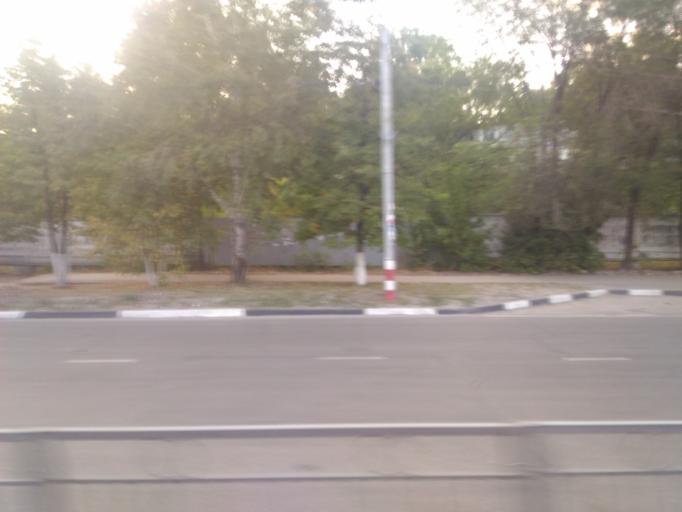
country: RU
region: Ulyanovsk
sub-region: Ulyanovskiy Rayon
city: Ulyanovsk
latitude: 54.2881
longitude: 48.3041
